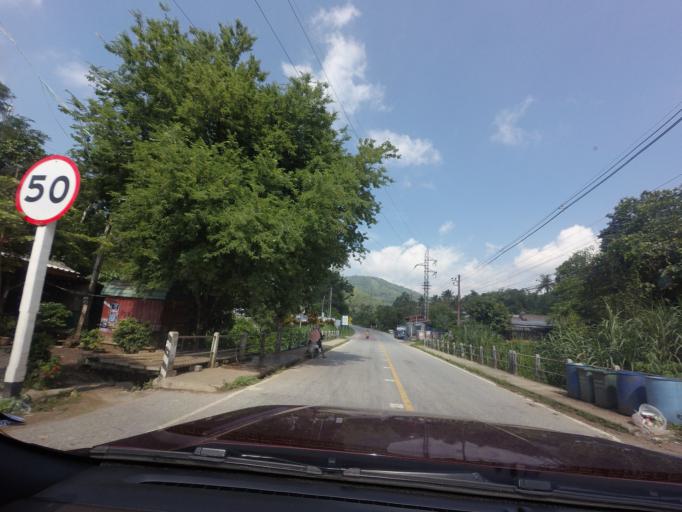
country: TH
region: Yala
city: Betong
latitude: 5.9195
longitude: 101.1790
